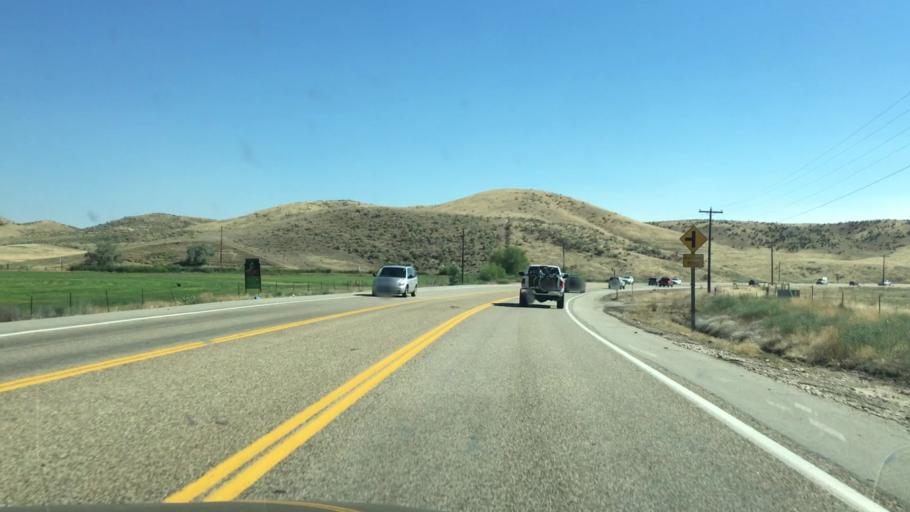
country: US
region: Idaho
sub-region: Ada County
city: Eagle
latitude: 43.7319
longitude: -116.3042
